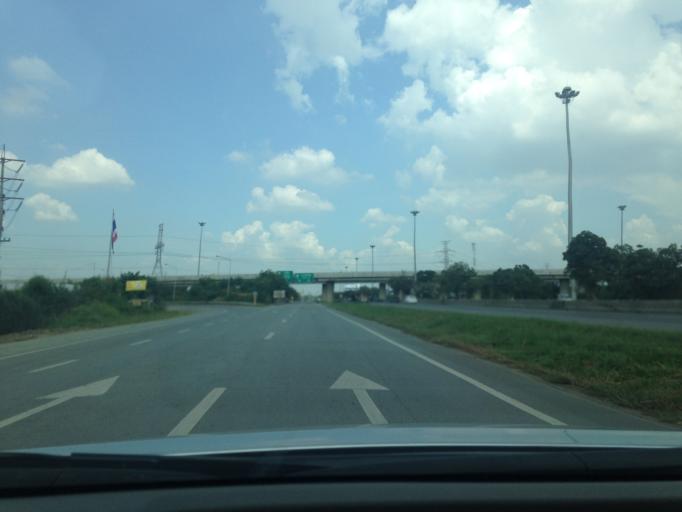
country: TH
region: Pathum Thani
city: Sam Khok
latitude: 14.0917
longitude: 100.5168
